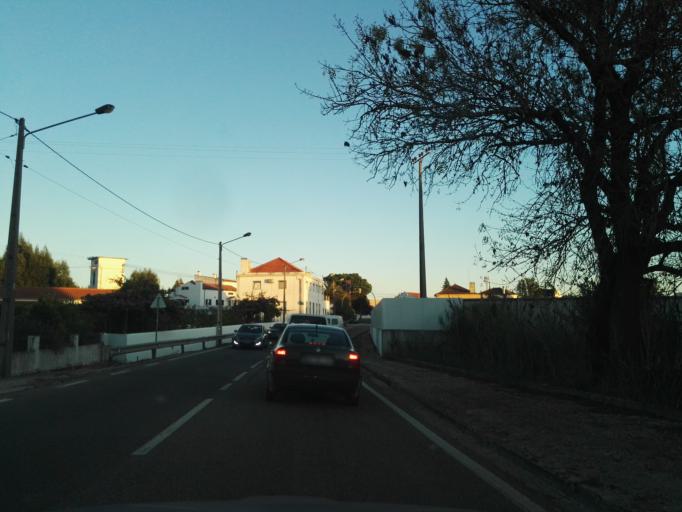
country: PT
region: Santarem
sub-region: Santarem
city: Santarem
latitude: 39.2705
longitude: -8.6984
